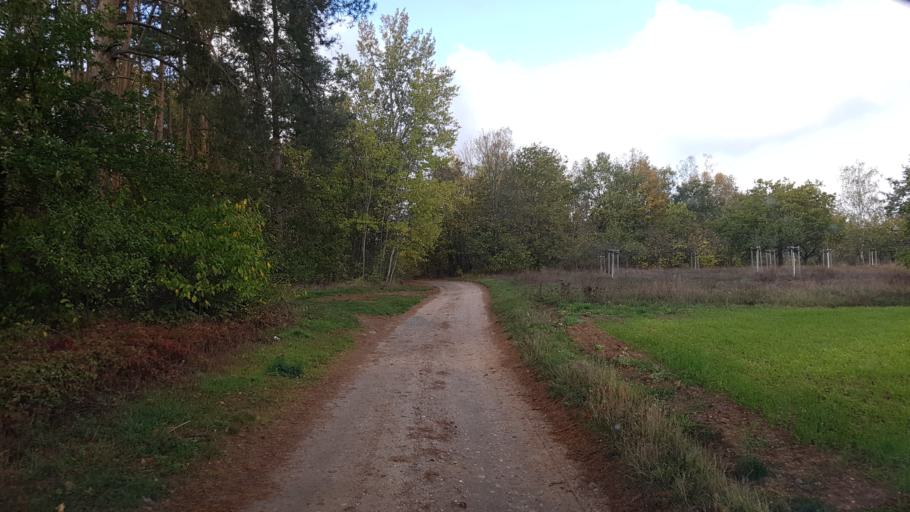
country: DE
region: Brandenburg
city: Doberlug-Kirchhain
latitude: 51.6336
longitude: 13.5352
